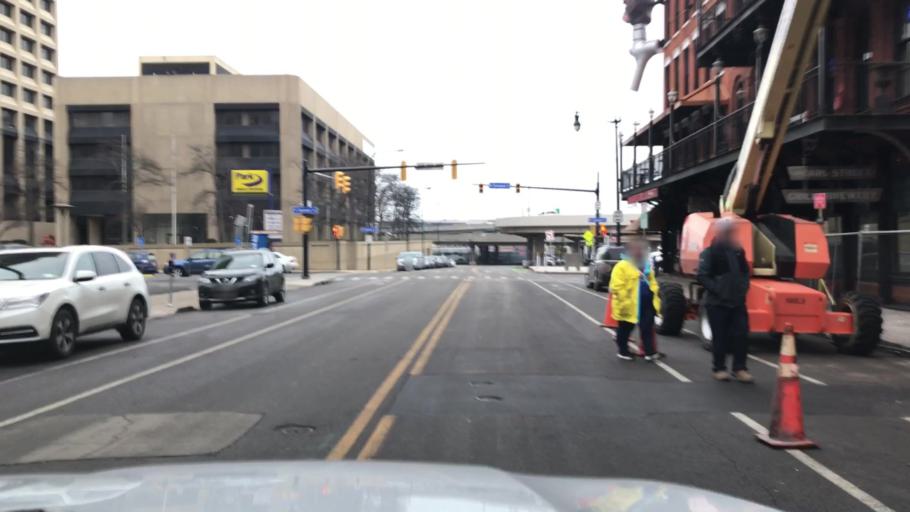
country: US
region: New York
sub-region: Erie County
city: Buffalo
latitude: 42.8813
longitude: -78.8770
